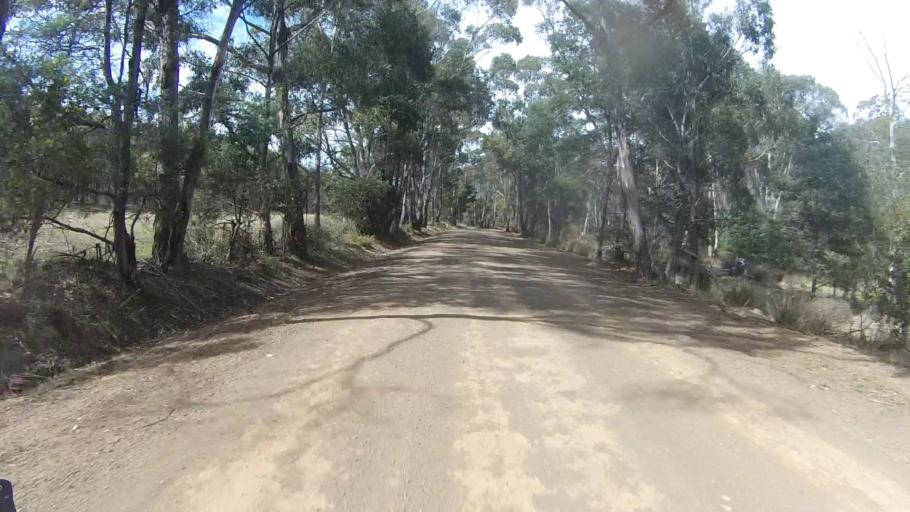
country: AU
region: Tasmania
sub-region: Sorell
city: Sorell
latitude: -42.6570
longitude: 147.8980
